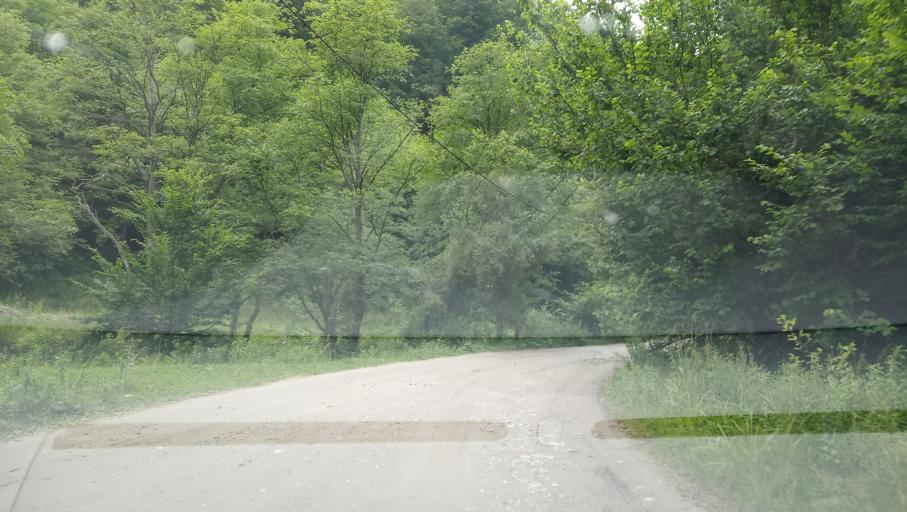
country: RO
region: Hunedoara
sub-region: Oras Petrila
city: Petrila
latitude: 45.4755
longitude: 23.4157
